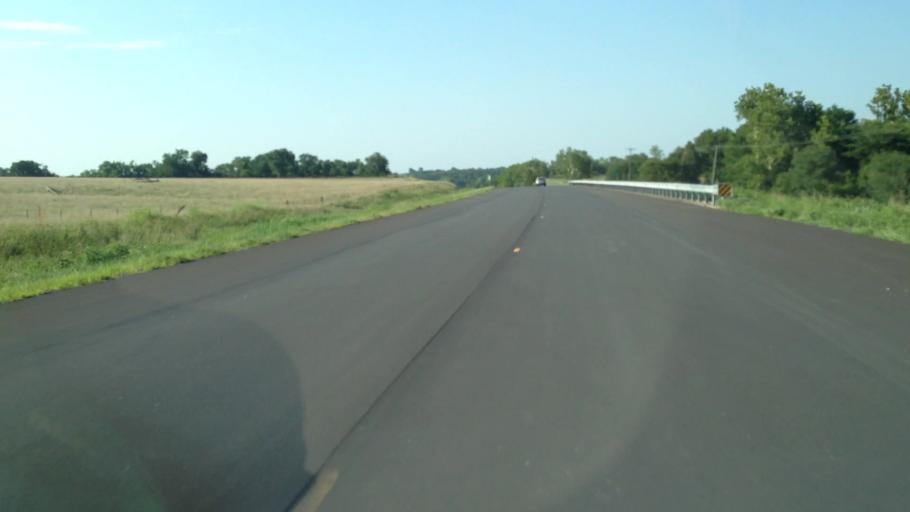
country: US
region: Kansas
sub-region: Anderson County
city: Garnett
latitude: 38.3275
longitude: -95.2495
